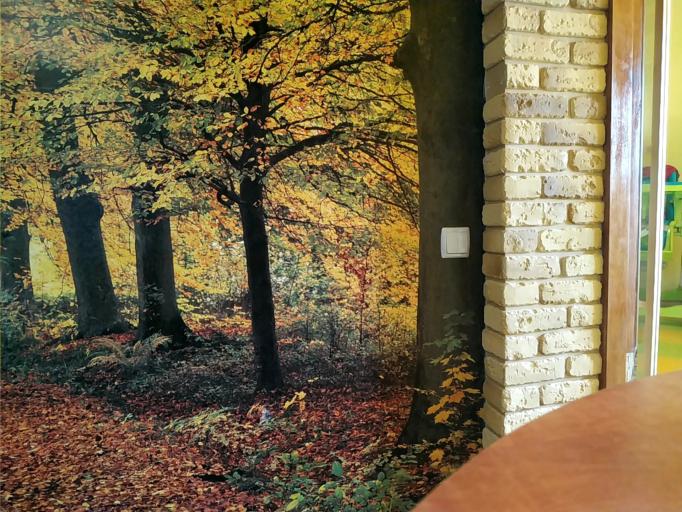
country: RU
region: Vologda
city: Nelazskoye
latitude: 59.4175
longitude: 37.6083
